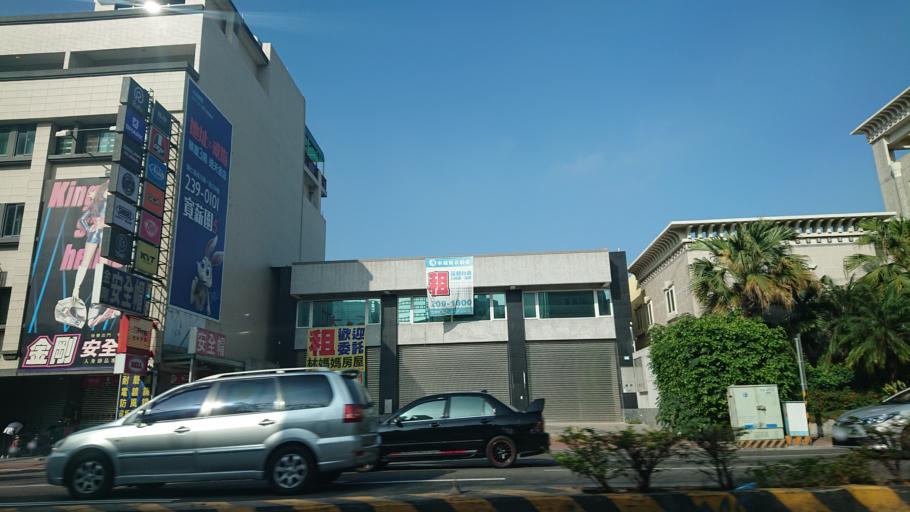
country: TW
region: Taiwan
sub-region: Tainan
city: Tainan
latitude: 22.9992
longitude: 120.1868
